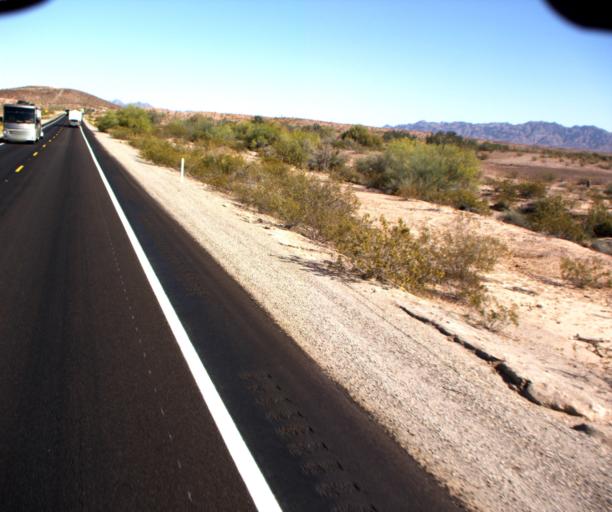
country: US
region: Arizona
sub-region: Yuma County
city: Wellton
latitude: 33.0941
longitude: -114.2976
